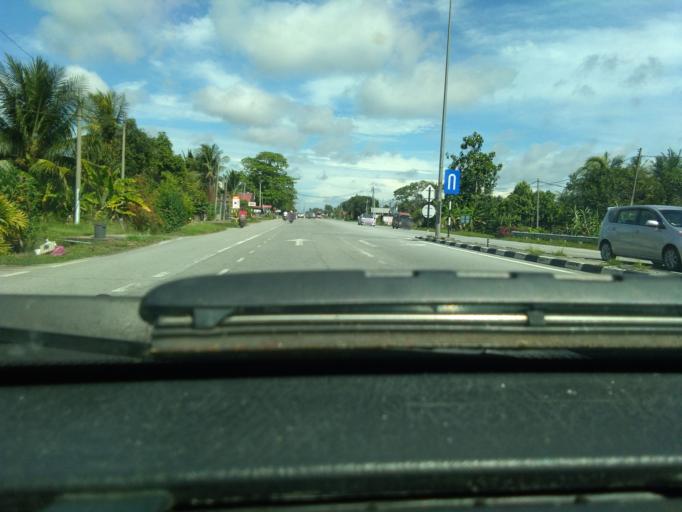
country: MY
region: Perak
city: Bagan Serai
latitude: 5.0024
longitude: 100.5499
